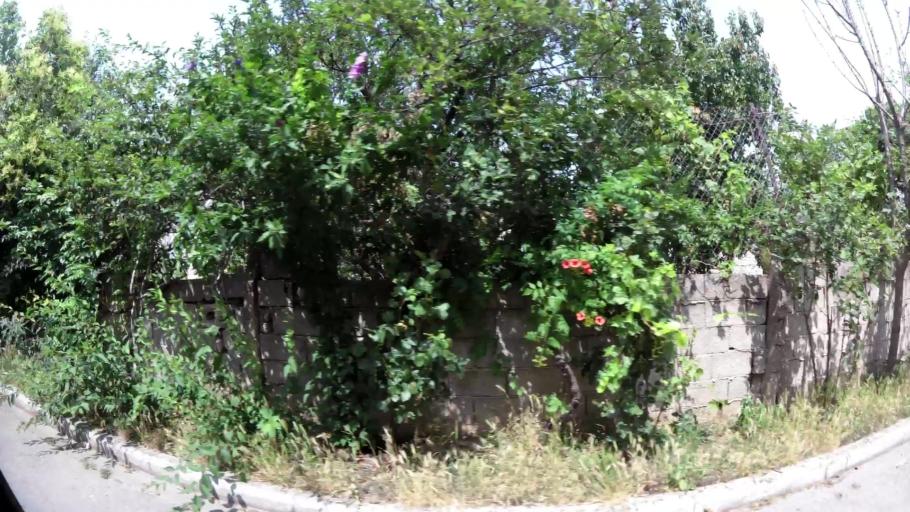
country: GR
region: Central Macedonia
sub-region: Nomos Thessalonikis
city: Diavata
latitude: 40.6919
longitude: 22.8576
